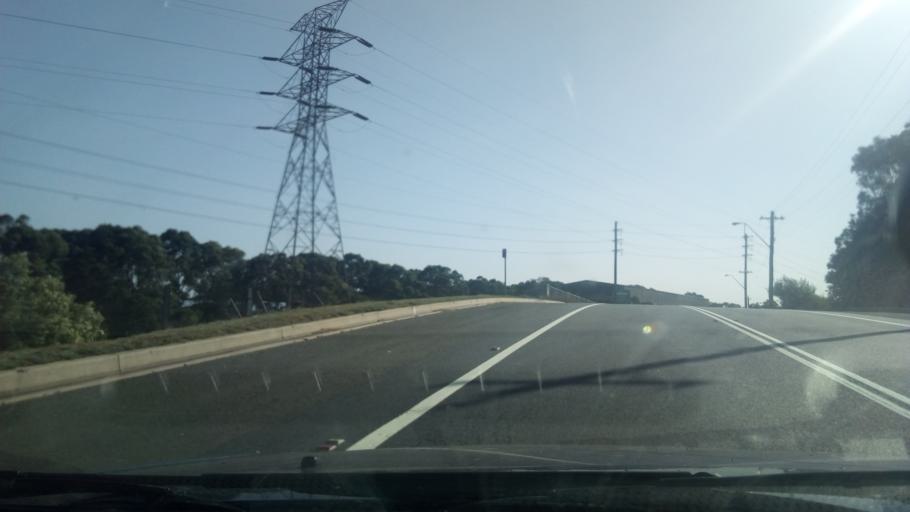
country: AU
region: New South Wales
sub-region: Wollongong
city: Cringila
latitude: -34.4725
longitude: 150.8899
